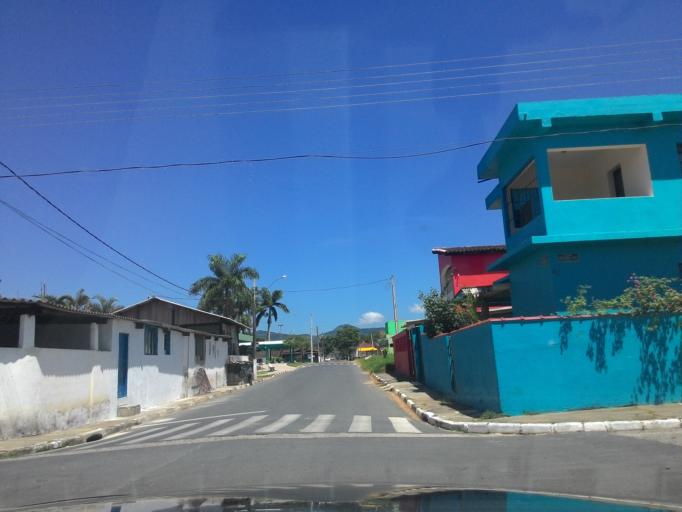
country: BR
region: Sao Paulo
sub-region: Pariquera-Acu
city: Pariquera Acu
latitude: -24.7133
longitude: -47.8849
